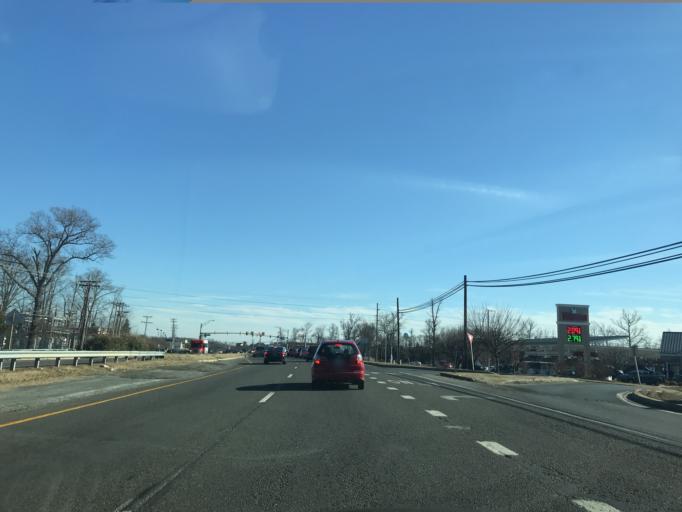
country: US
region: Maryland
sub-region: Charles County
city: Waldorf
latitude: 38.6308
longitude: -76.9193
